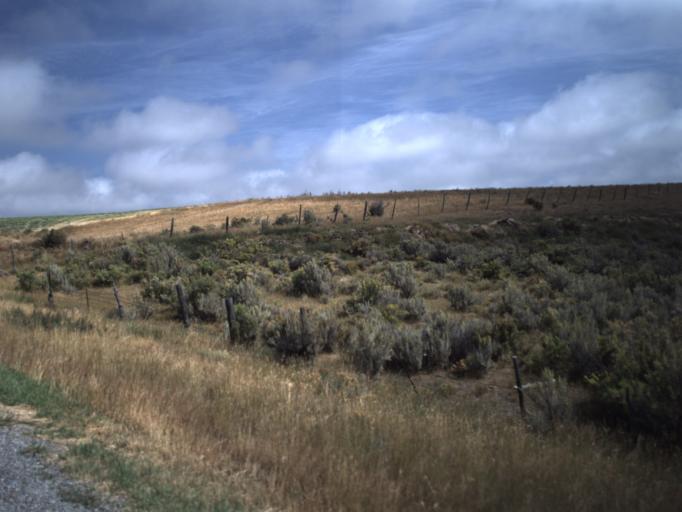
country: US
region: Utah
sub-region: Rich County
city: Randolph
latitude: 41.7265
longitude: -111.1591
